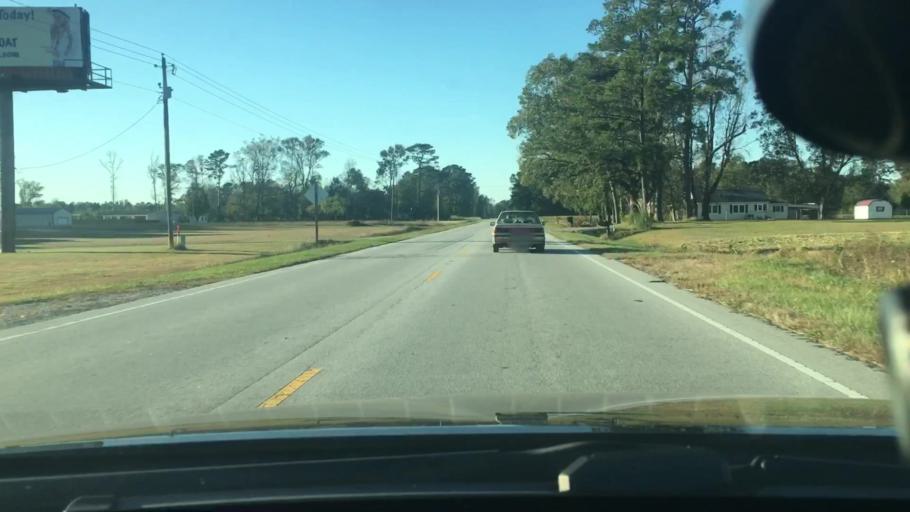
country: US
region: North Carolina
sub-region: Craven County
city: Vanceboro
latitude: 35.2717
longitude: -77.1130
